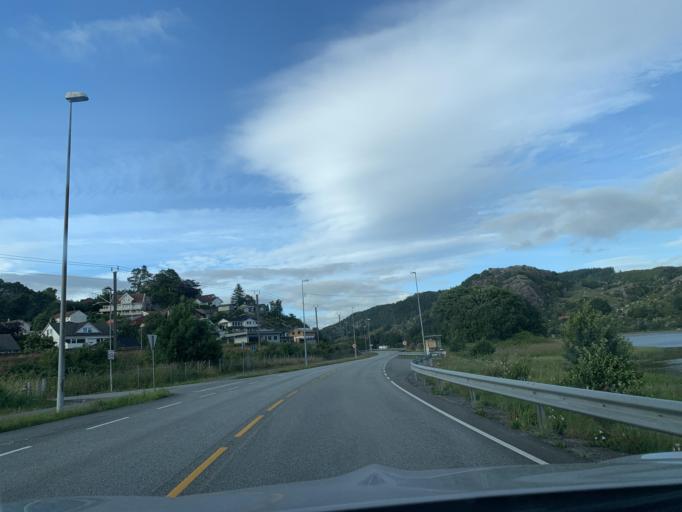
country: NO
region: Rogaland
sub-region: Eigersund
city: Egersund
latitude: 58.4624
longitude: 6.0179
